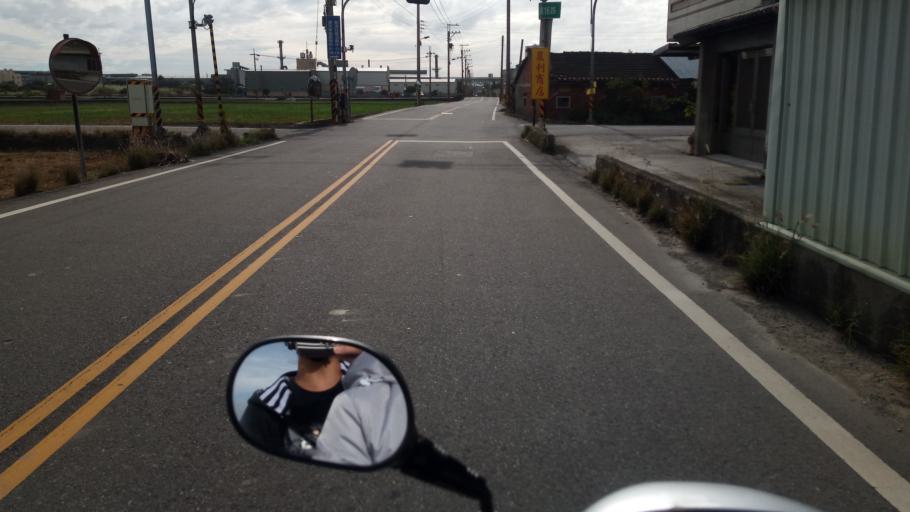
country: TW
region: Taiwan
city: Fengyuan
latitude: 24.4156
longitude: 120.6507
